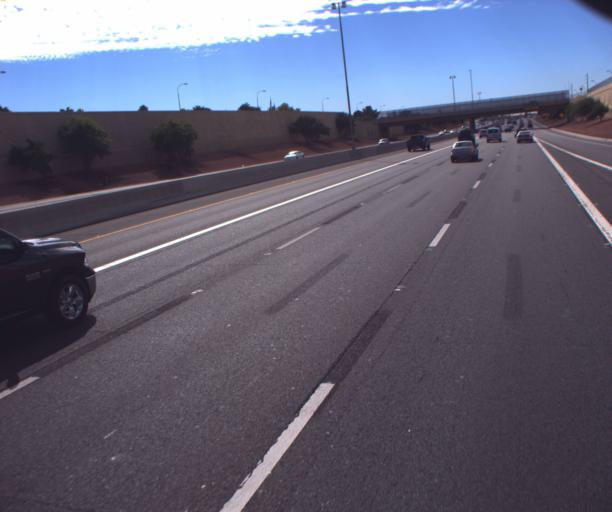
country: US
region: Arizona
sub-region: Maricopa County
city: San Carlos
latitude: 33.3450
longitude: -111.8937
